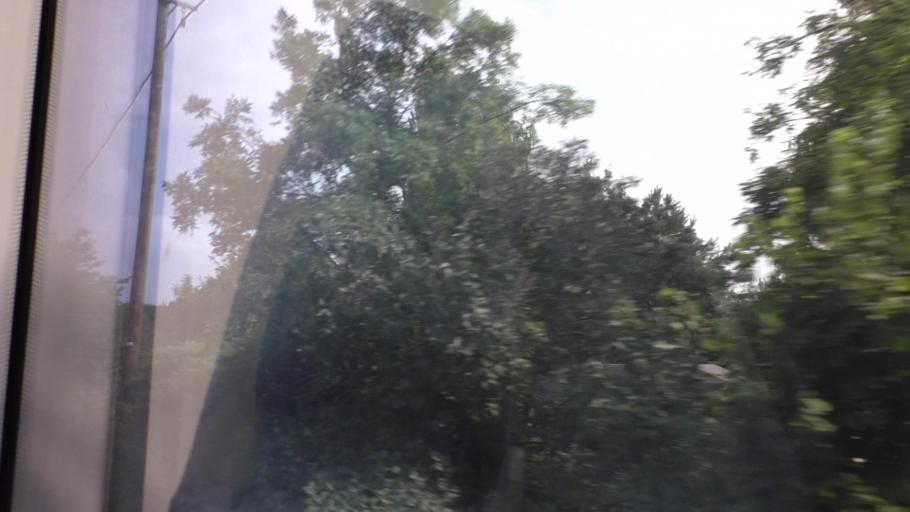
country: DE
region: Brandenburg
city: Bestensee
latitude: 52.2999
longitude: 13.7239
